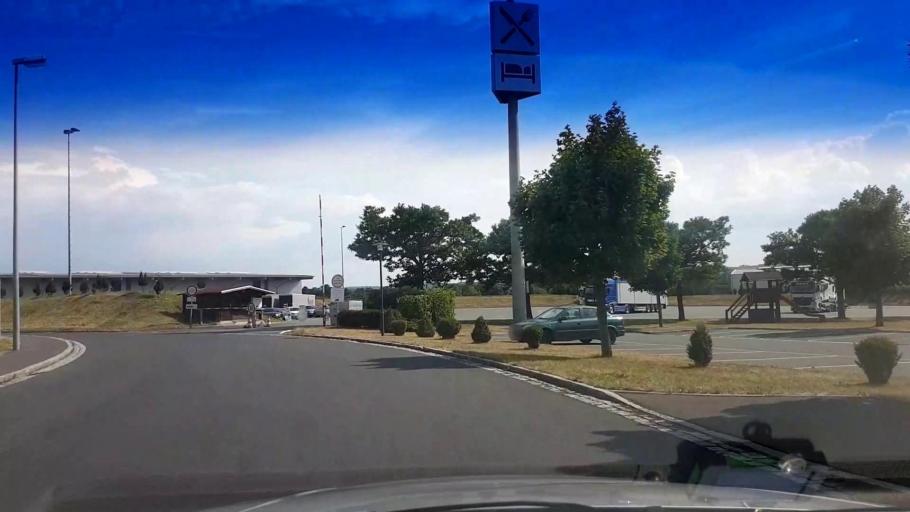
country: DE
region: Bavaria
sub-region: Upper Franconia
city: Himmelkron
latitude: 50.0525
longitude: 11.6222
